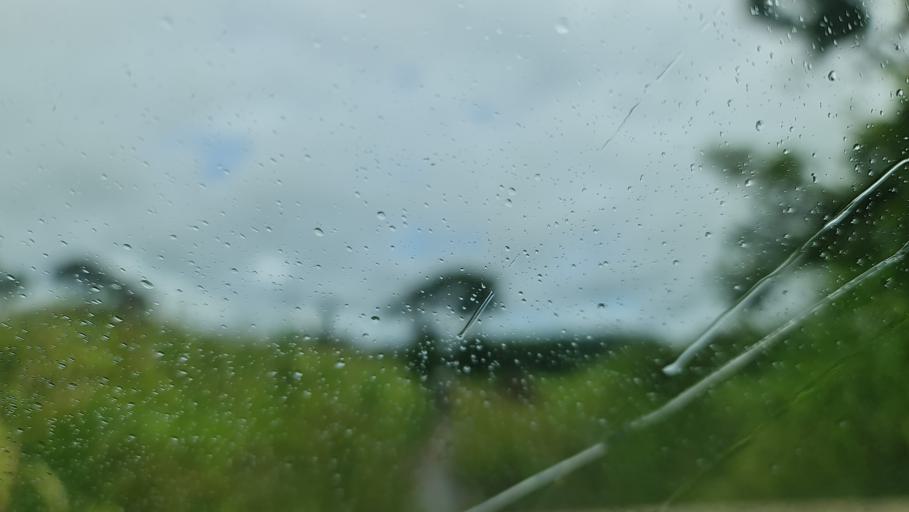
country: MW
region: Southern Region
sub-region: Nsanje District
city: Nsanje
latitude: -17.4468
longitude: 35.8429
